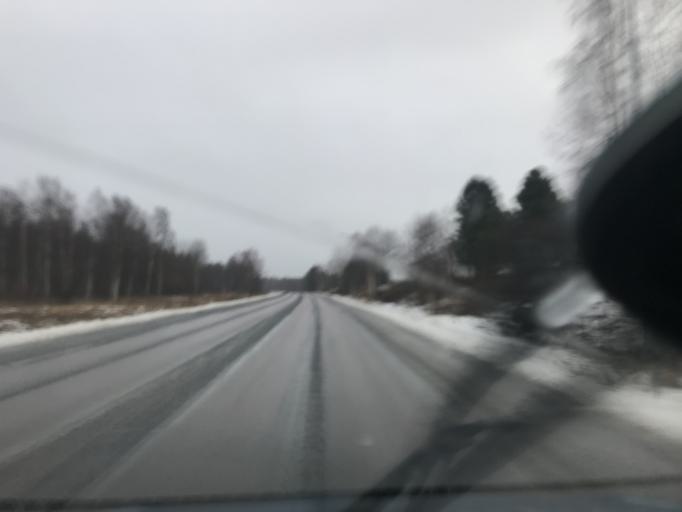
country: SE
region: Norrbotten
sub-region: Lulea Kommun
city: Sodra Sunderbyn
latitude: 65.6575
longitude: 21.9608
